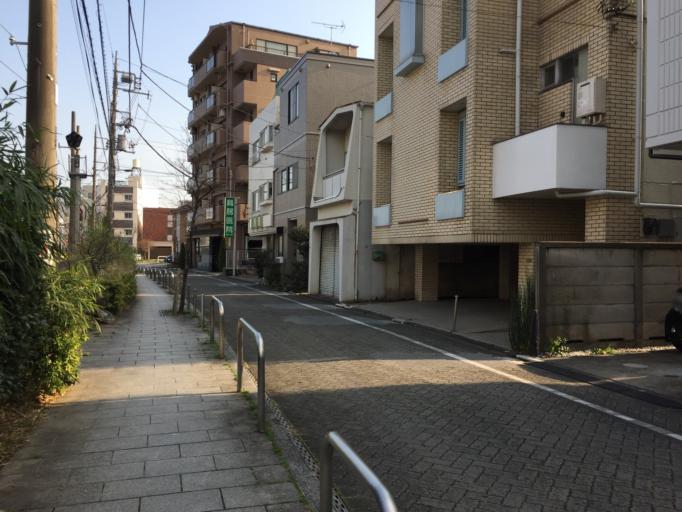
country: JP
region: Tokyo
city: Tokyo
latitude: 35.6586
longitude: 139.6423
